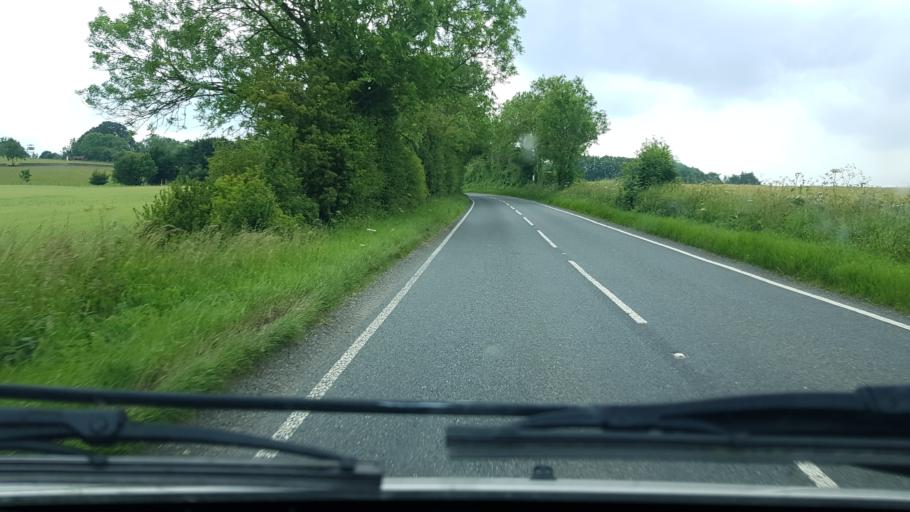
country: GB
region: England
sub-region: Gloucestershire
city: Donnington
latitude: 51.9439
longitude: -1.7305
